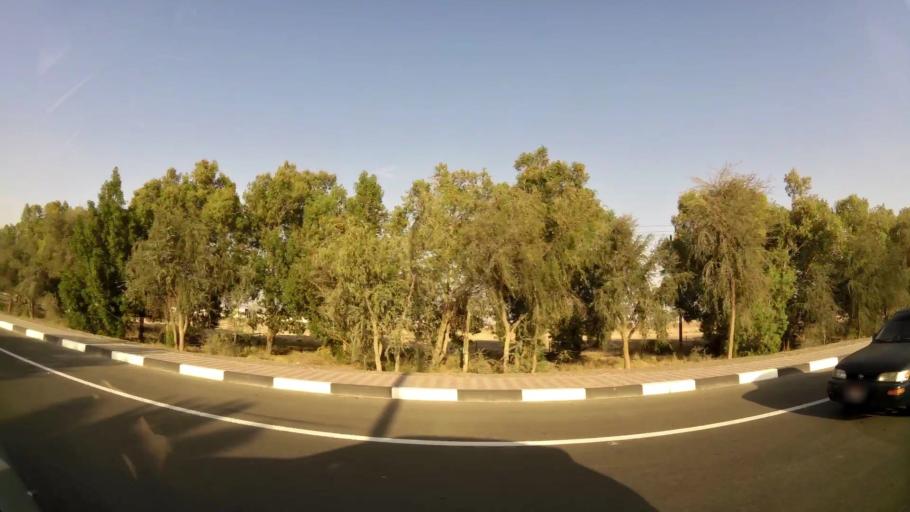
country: AE
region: Abu Dhabi
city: Al Ain
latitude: 24.1268
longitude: 55.8215
